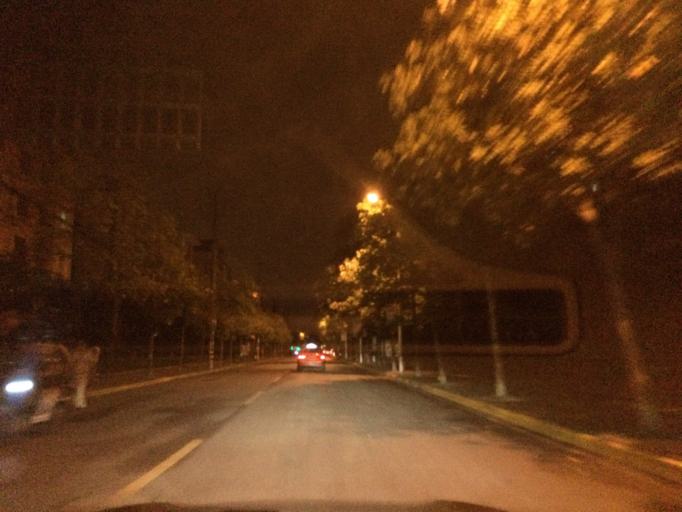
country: CN
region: Shanghai Shi
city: Baoshan
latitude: 31.4074
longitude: 121.4884
